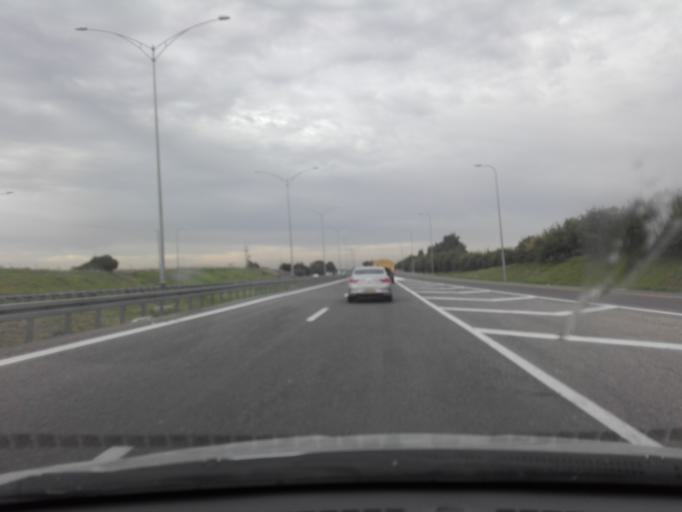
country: IL
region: Central District
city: Mazkeret Batya
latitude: 31.8791
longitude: 34.8776
